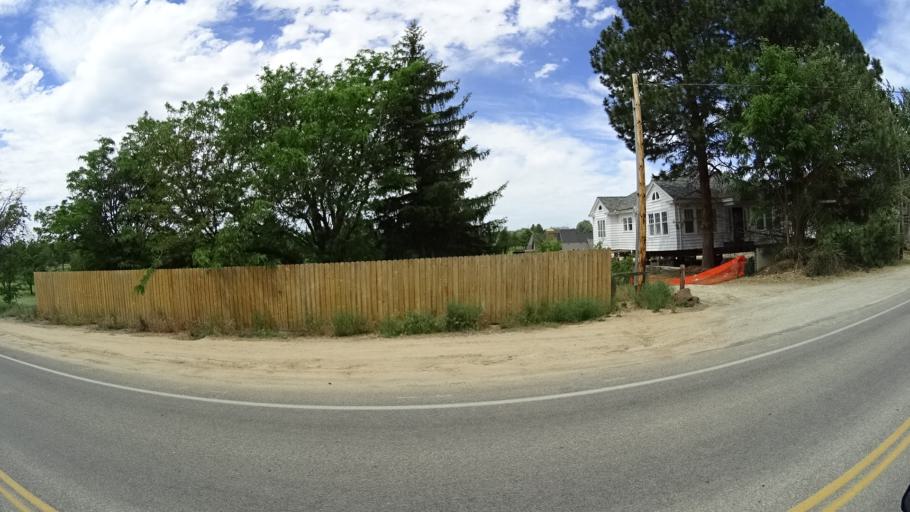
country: US
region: Idaho
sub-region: Ada County
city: Boise
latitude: 43.5954
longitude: -116.1632
